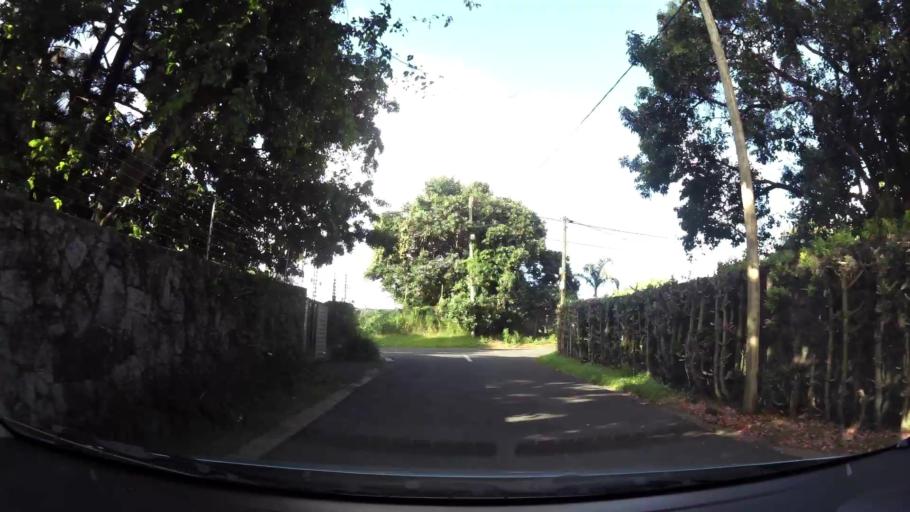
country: MU
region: Plaines Wilhems
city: Vacoas
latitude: -20.3073
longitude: 57.4982
